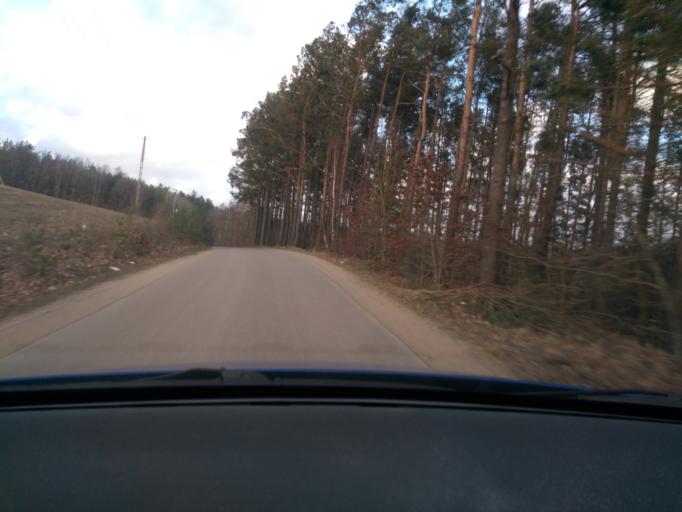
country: PL
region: Pomeranian Voivodeship
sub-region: Powiat kartuski
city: Przodkowo
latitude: 54.4129
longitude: 18.2371
